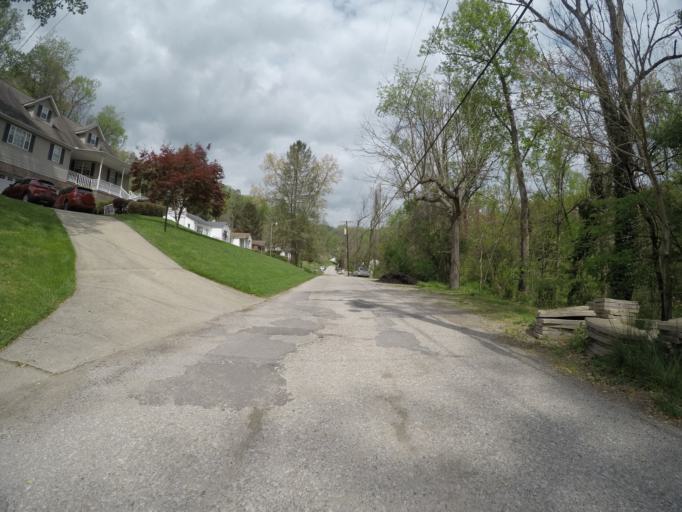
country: US
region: West Virginia
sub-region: Kanawha County
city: Charleston
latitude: 38.3876
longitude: -81.6053
